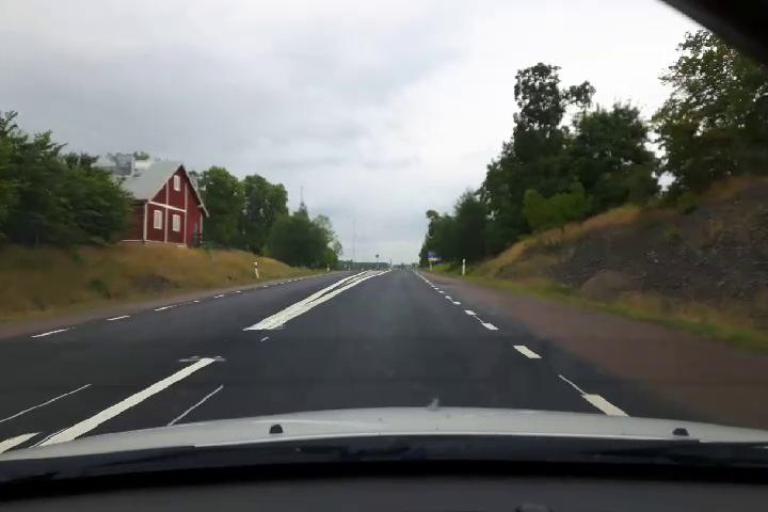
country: SE
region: Uppsala
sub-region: Uppsala Kommun
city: Gamla Uppsala
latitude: 59.9013
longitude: 17.6119
